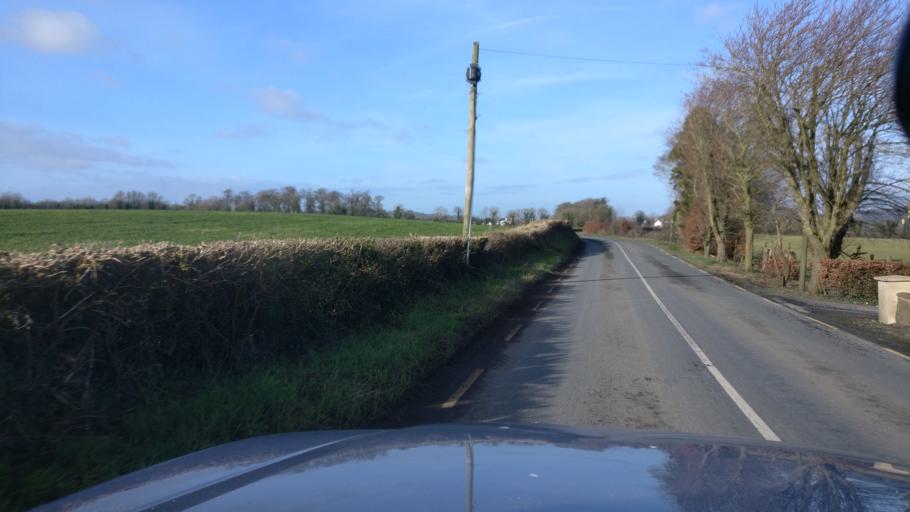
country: IE
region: Leinster
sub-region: Laois
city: Stradbally
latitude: 52.9721
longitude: -7.2126
